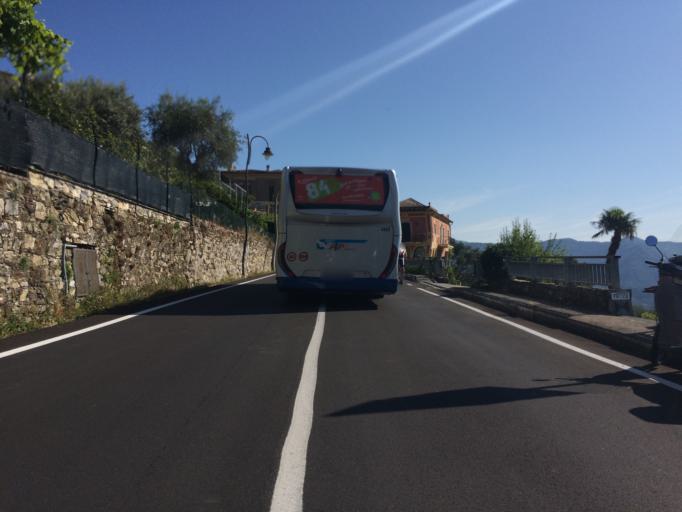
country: IT
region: Liguria
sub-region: Provincia di Genova
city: Camogli
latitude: 44.3420
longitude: 9.1824
